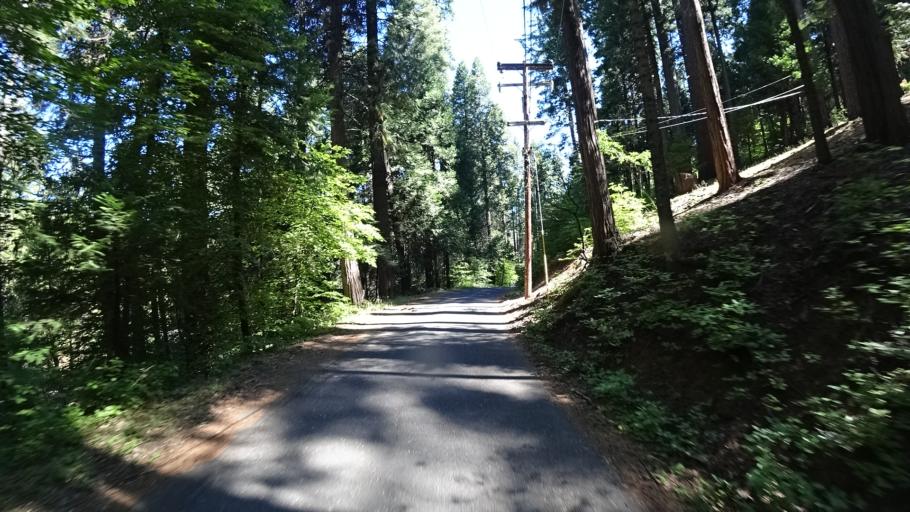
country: US
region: California
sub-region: Calaveras County
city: Arnold
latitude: 38.2463
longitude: -120.3316
